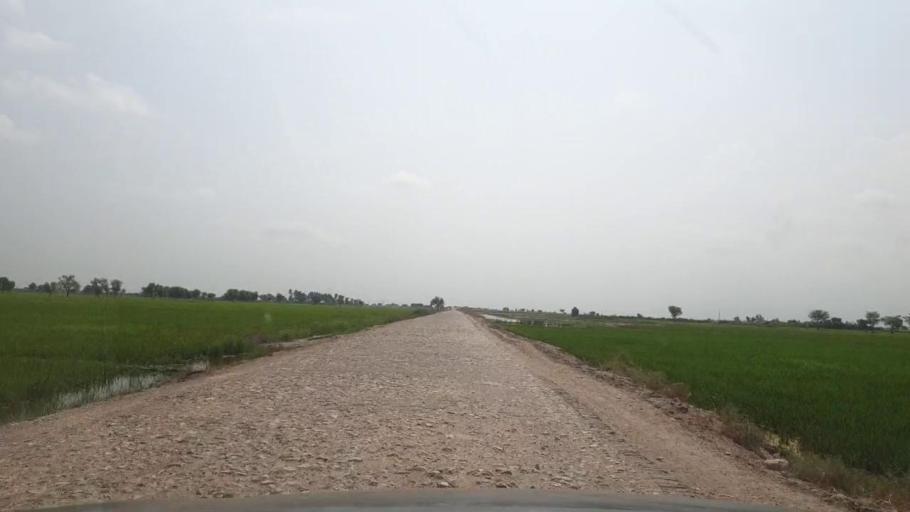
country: PK
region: Sindh
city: Ratodero
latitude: 27.8401
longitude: 68.3284
